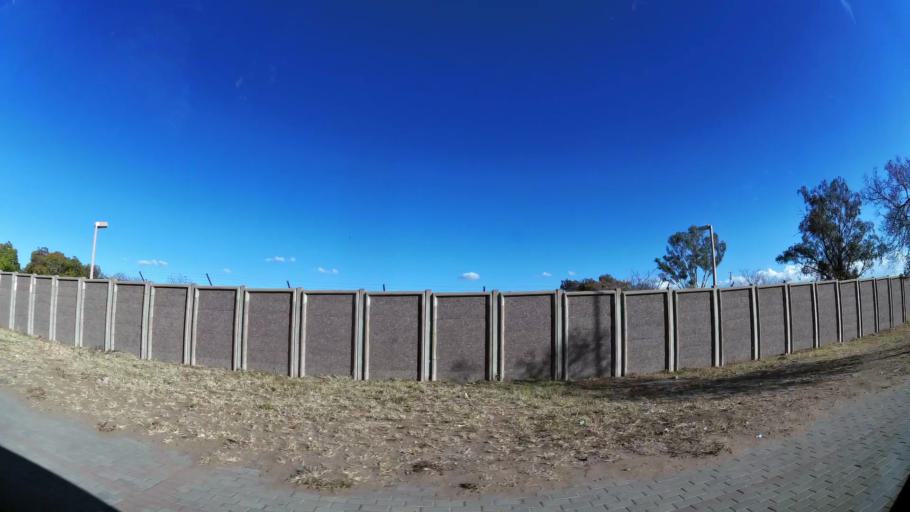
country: ZA
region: Limpopo
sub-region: Capricorn District Municipality
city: Polokwane
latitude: -23.8970
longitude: 29.4604
